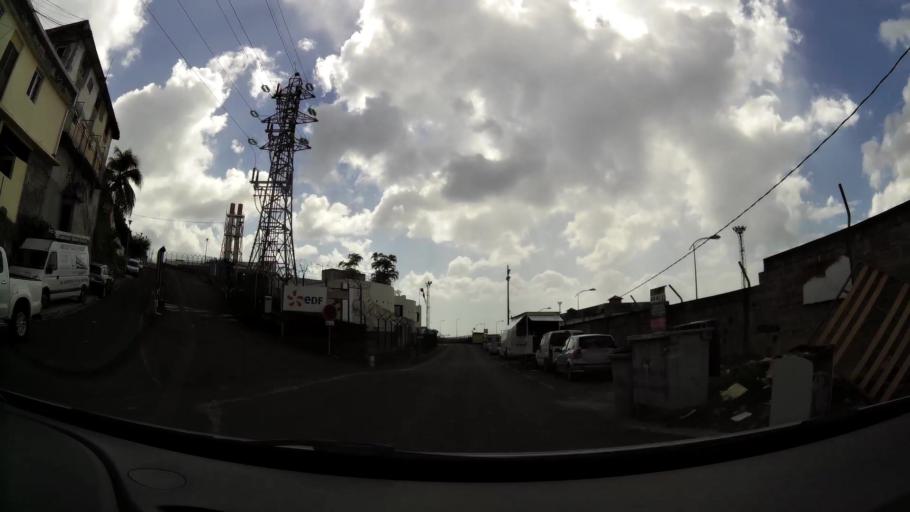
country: MQ
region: Martinique
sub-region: Martinique
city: Fort-de-France
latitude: 14.5992
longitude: -61.0582
